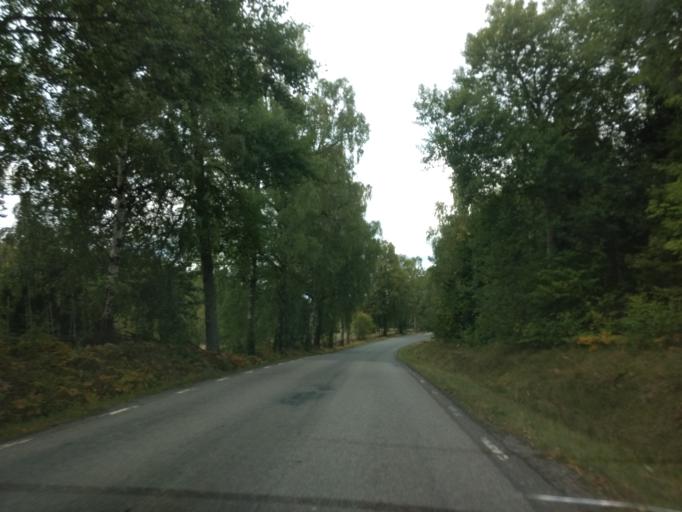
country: SE
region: Uppsala
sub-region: Habo Kommun
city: Balsta
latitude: 59.6915
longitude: 17.5331
